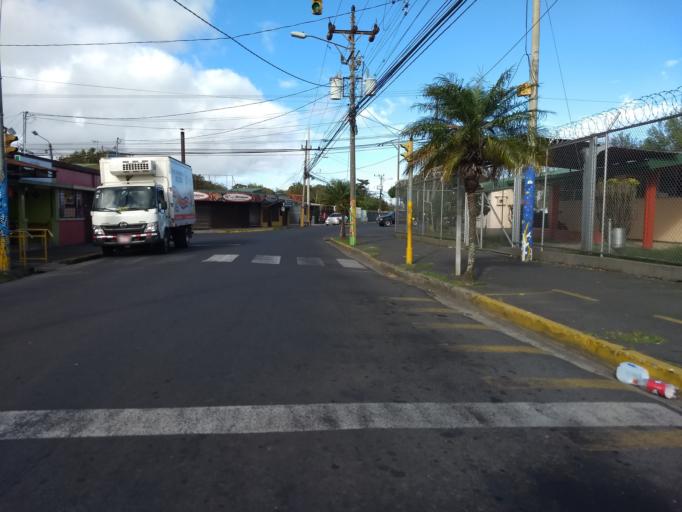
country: CR
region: San Jose
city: Calle Blancos
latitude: 9.9633
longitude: -84.0653
